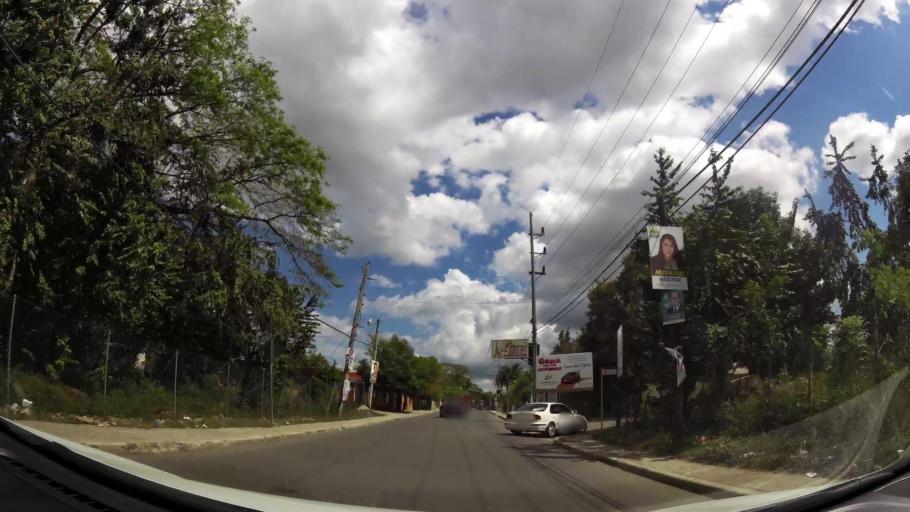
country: DO
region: Santiago
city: Santiago de los Caballeros
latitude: 19.4055
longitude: -70.6627
